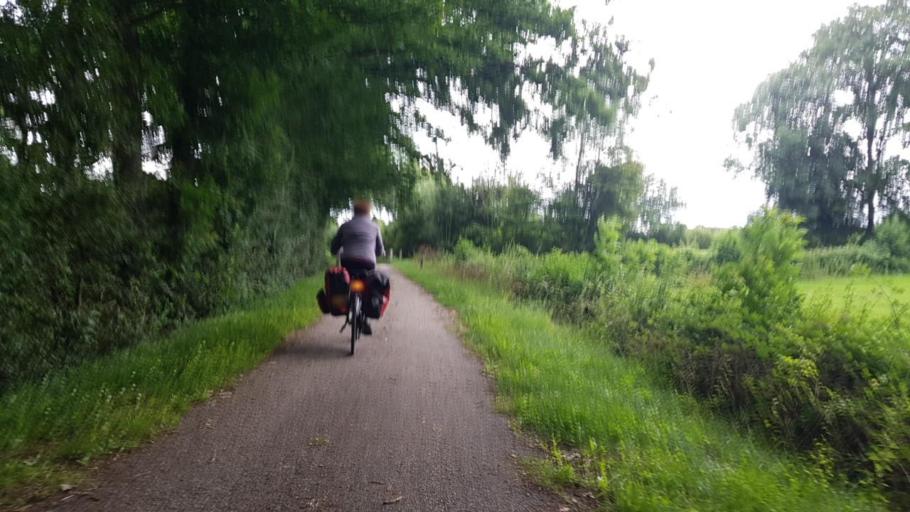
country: FR
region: Picardie
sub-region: Departement de l'Aisne
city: Buironfosse
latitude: 49.9028
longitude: 3.8390
